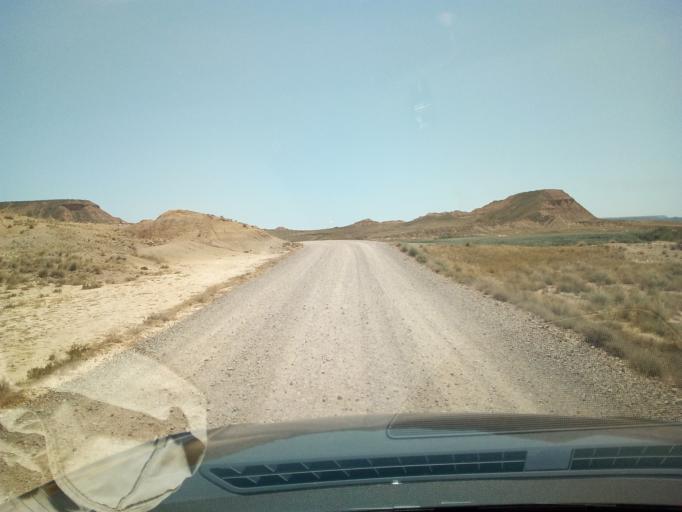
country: ES
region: Navarre
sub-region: Provincia de Navarra
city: Arguedas
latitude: 42.2072
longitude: -1.5096
